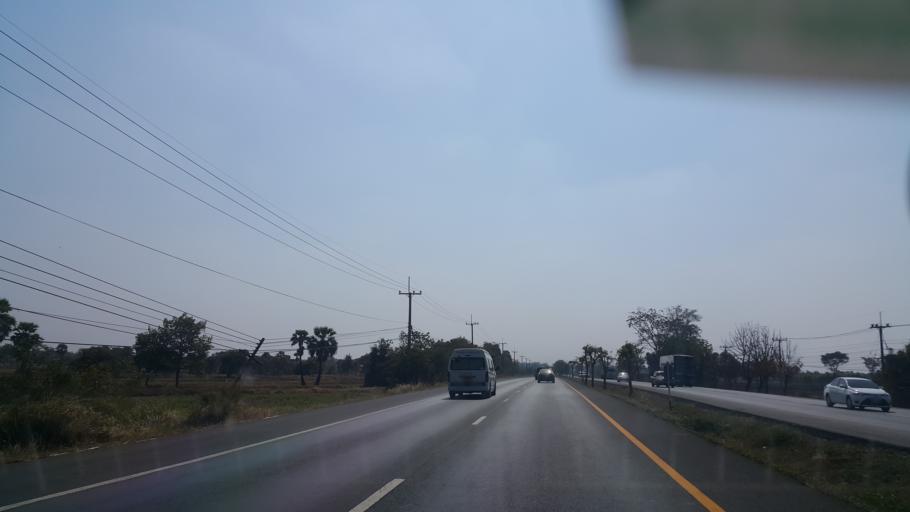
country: TH
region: Nakhon Ratchasima
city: Non Daeng
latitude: 15.4270
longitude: 102.4867
